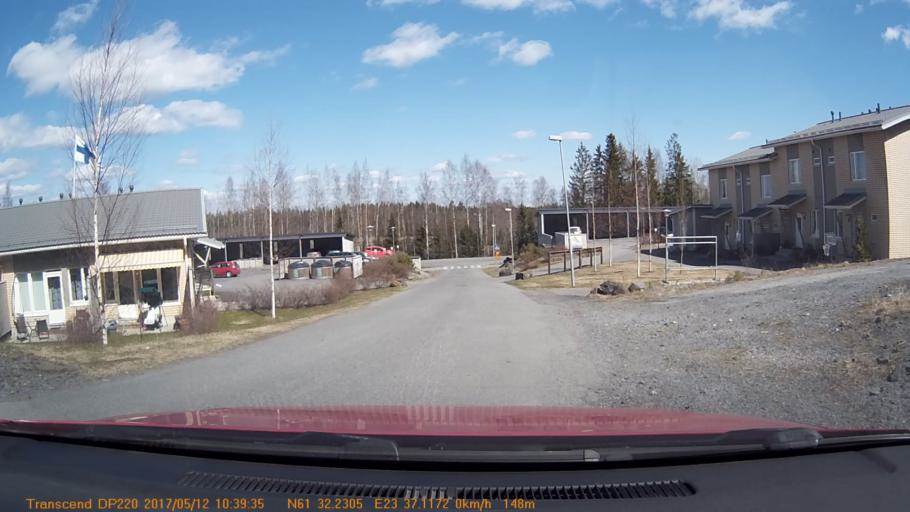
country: FI
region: Pirkanmaa
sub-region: Tampere
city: Yloejaervi
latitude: 61.5372
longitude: 23.6186
